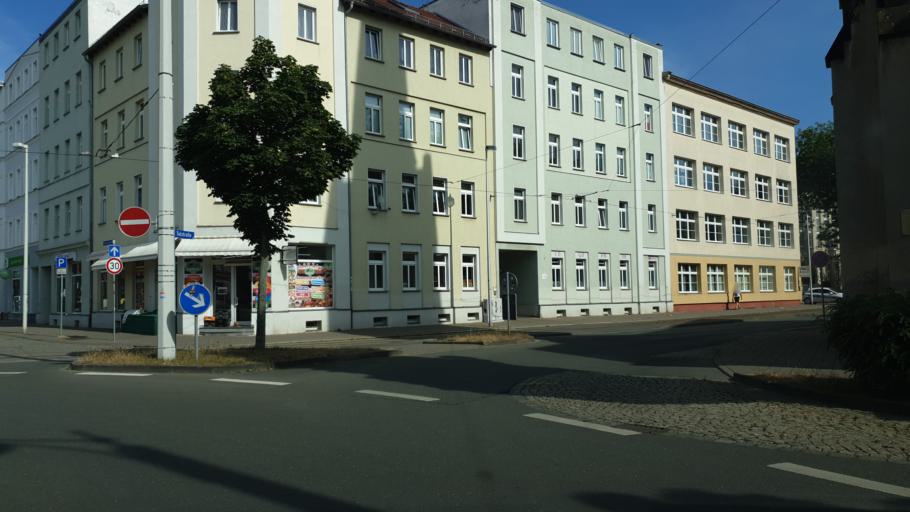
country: DE
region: Thuringia
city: Gera
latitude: 50.8745
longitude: 12.0773
